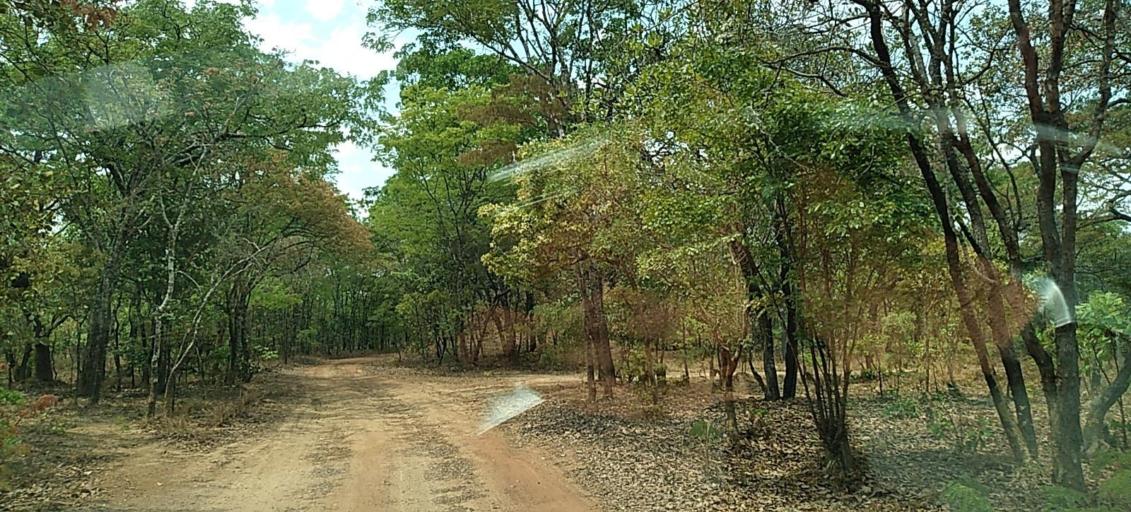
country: ZM
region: Copperbelt
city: Chililabombwe
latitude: -12.5030
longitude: 27.6373
